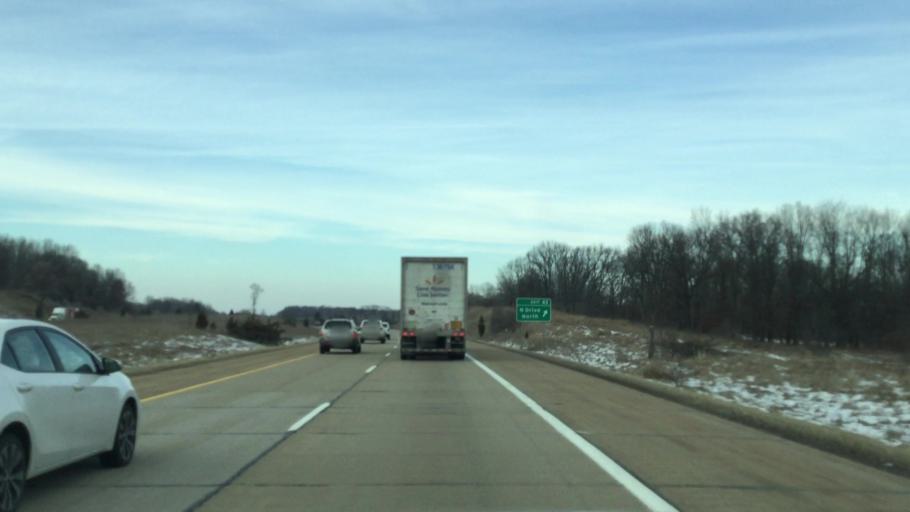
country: US
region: Michigan
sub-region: Calhoun County
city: Marshall
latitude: 42.3419
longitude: -84.9816
